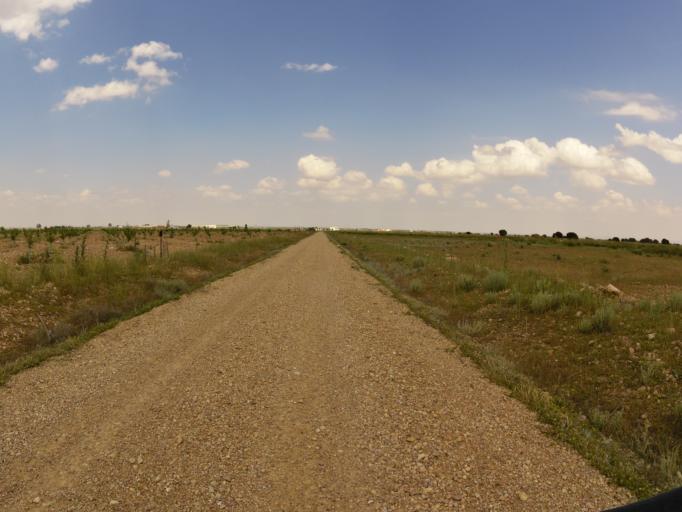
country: ES
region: Castille-La Mancha
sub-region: Provincia de Albacete
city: Balazote
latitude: 38.8871
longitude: -2.1222
